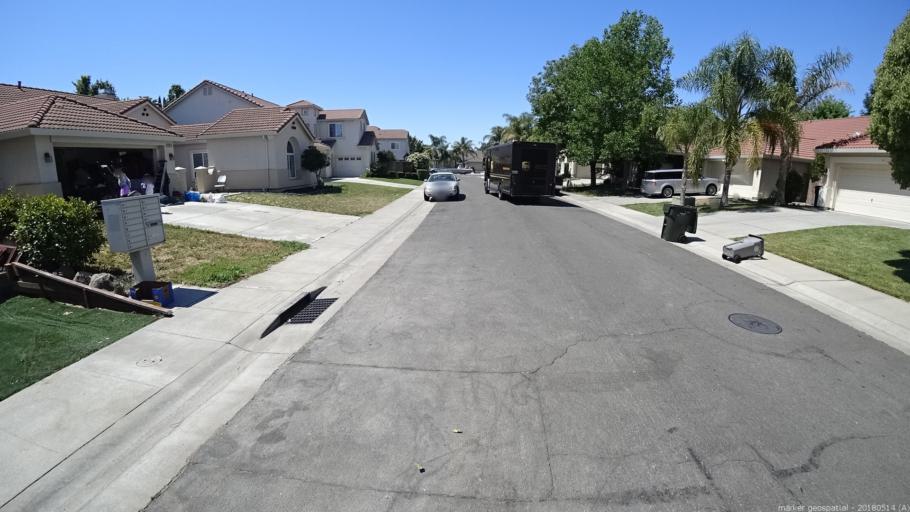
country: US
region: California
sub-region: Yolo County
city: West Sacramento
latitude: 38.6347
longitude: -121.5314
